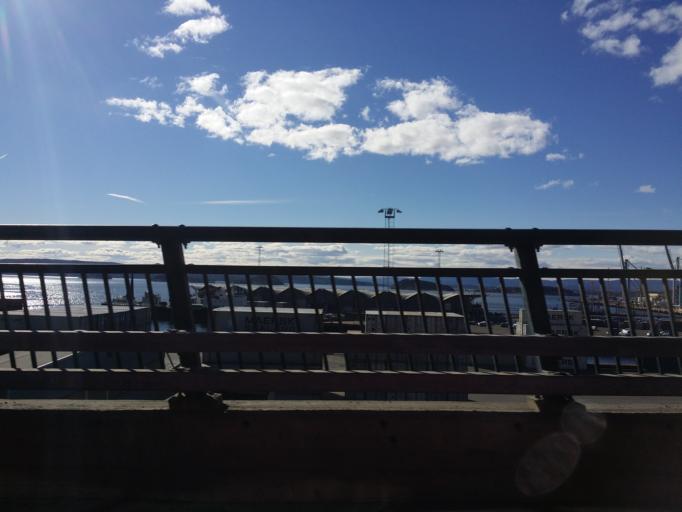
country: NO
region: Oslo
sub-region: Oslo
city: Oslo
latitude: 59.8856
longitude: 10.7680
